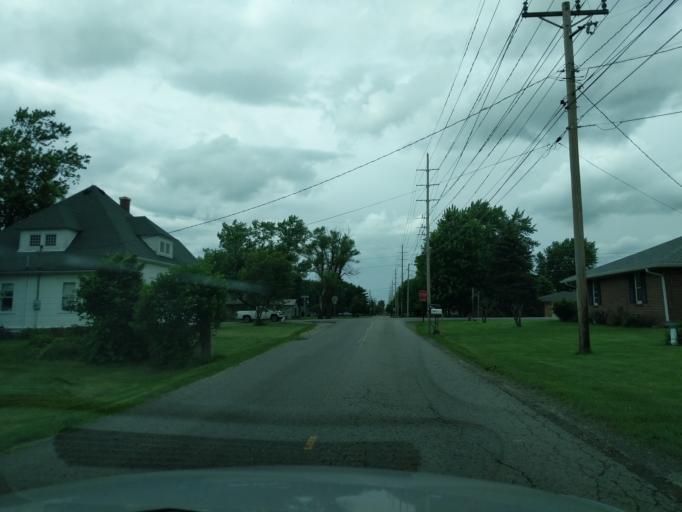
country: US
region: Indiana
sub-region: Madison County
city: Edgewood
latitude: 40.0607
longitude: -85.7302
